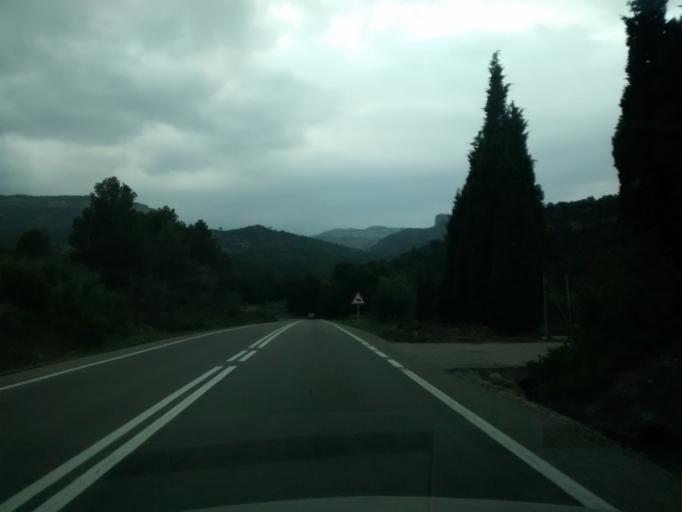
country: ES
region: Catalonia
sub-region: Provincia de Tarragona
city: Benifallet
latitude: 41.0199
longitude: 0.5011
